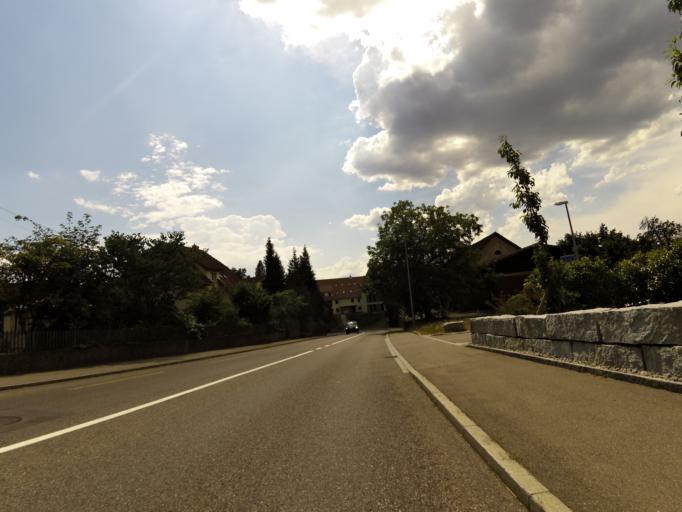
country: CH
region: Aargau
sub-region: Bezirk Lenzburg
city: Othmarsingen
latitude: 47.4032
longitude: 8.2183
